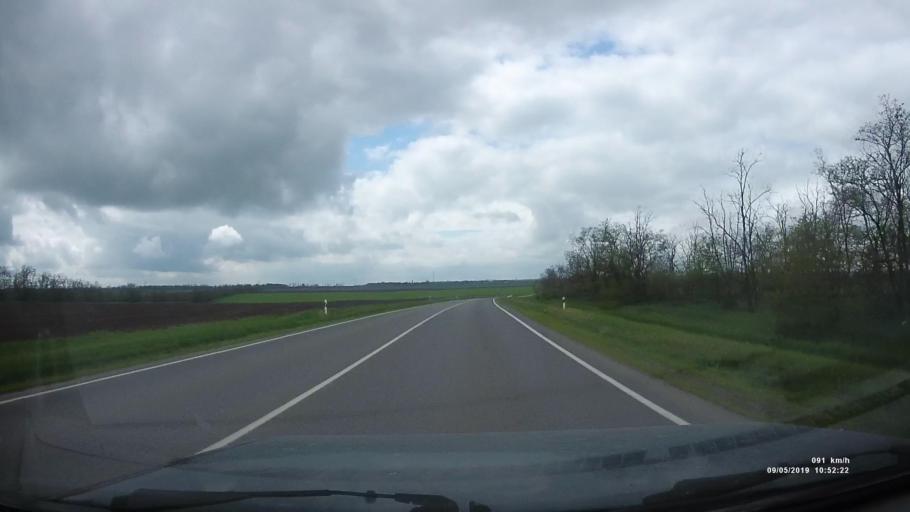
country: RU
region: Rostov
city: Peshkovo
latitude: 46.9018
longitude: 39.3536
